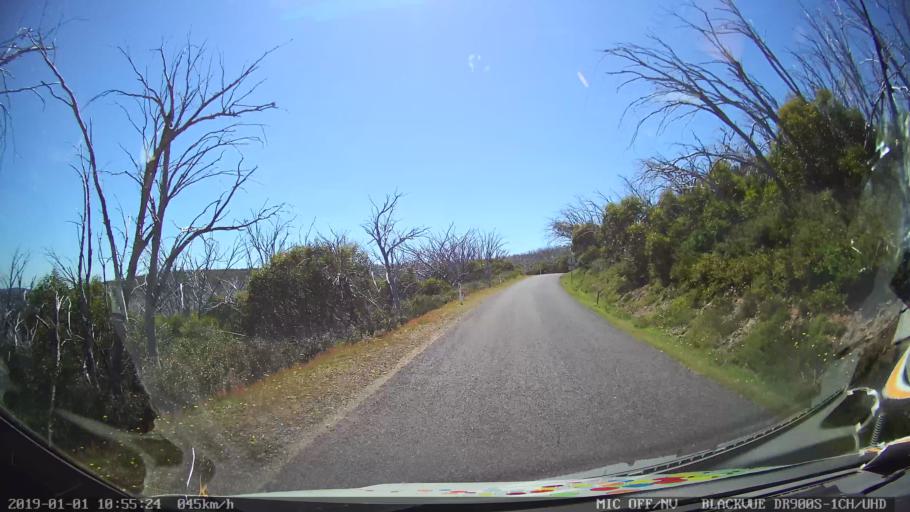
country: AU
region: New South Wales
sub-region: Snowy River
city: Jindabyne
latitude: -36.0082
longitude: 148.3883
